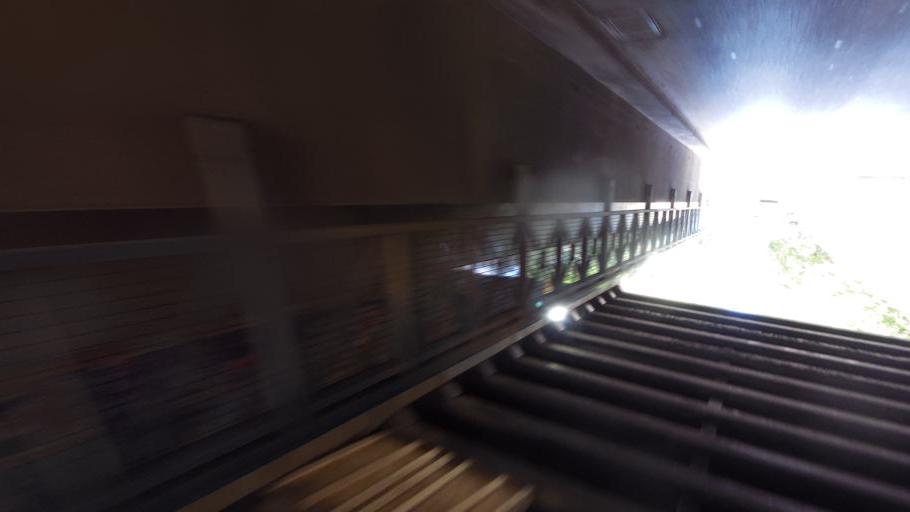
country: CA
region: British Columbia
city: Coquitlam
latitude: 49.2645
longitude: -122.7794
